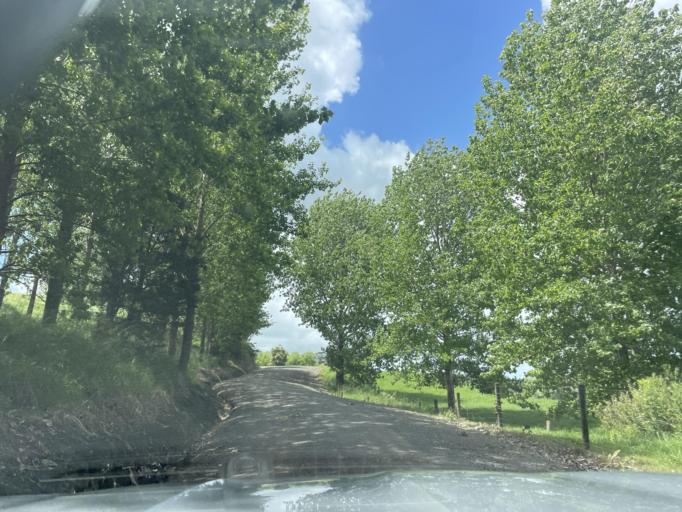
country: NZ
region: Auckland
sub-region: Auckland
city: Wellsford
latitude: -36.1746
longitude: 174.3162
